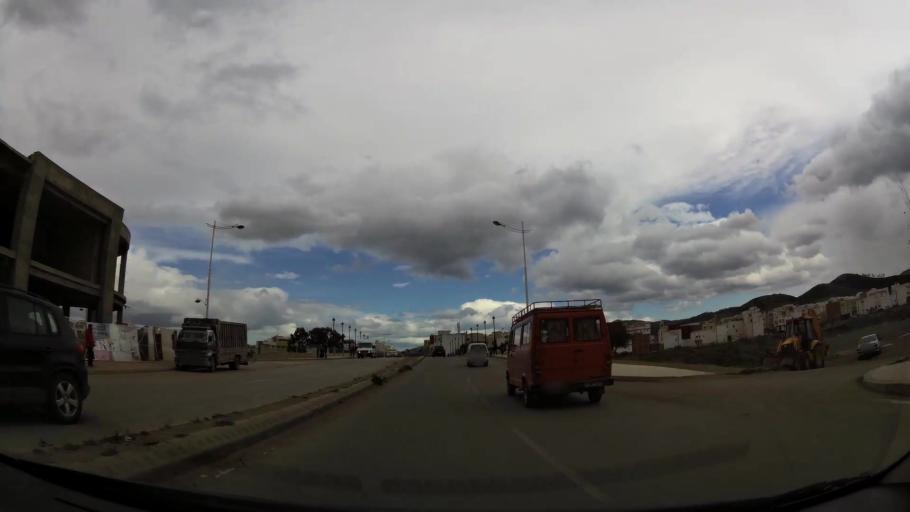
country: MA
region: Tanger-Tetouan
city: Tetouan
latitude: 35.5646
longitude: -5.3509
